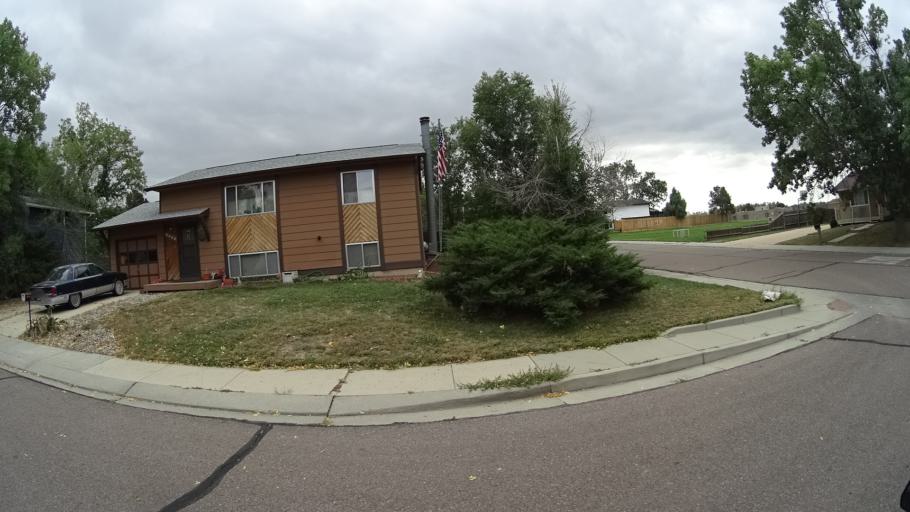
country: US
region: Colorado
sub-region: El Paso County
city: Cimarron Hills
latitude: 38.8908
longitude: -104.7422
